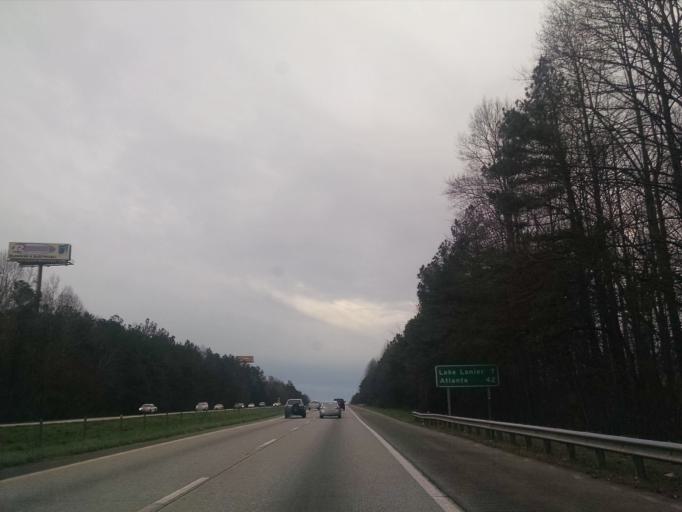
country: US
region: Georgia
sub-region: Hall County
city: Flowery Branch
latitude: 34.1683
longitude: -83.9229
